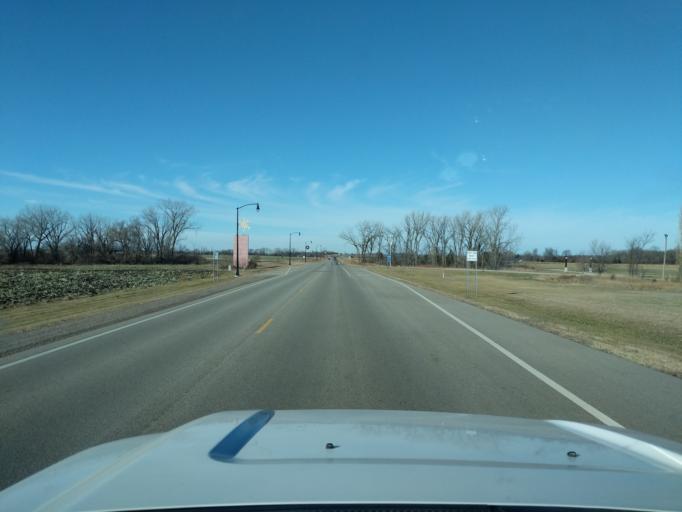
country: US
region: Minnesota
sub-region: Yellow Medicine County
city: Granite Falls
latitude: 44.7664
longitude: -95.5347
